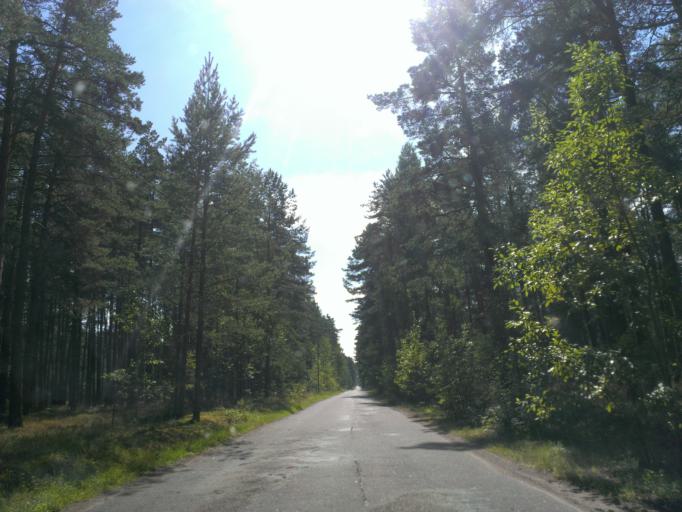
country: LV
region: Adazi
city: Adazi
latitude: 57.1201
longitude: 24.3455
